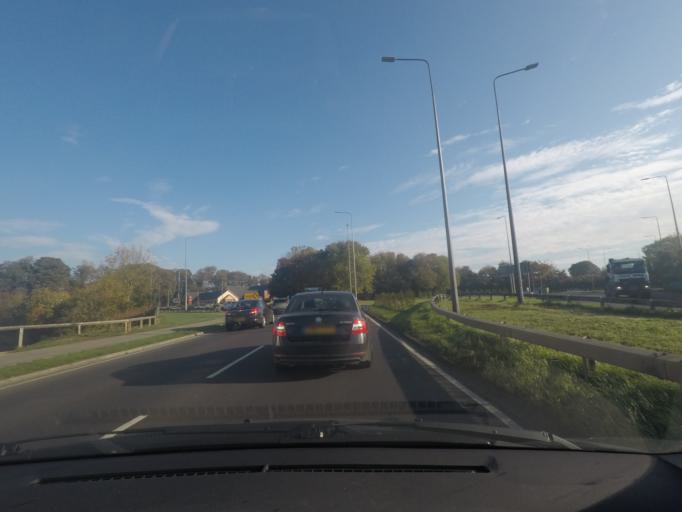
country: GB
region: England
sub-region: East Riding of Yorkshire
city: Hessle
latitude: 53.7245
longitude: -0.4587
